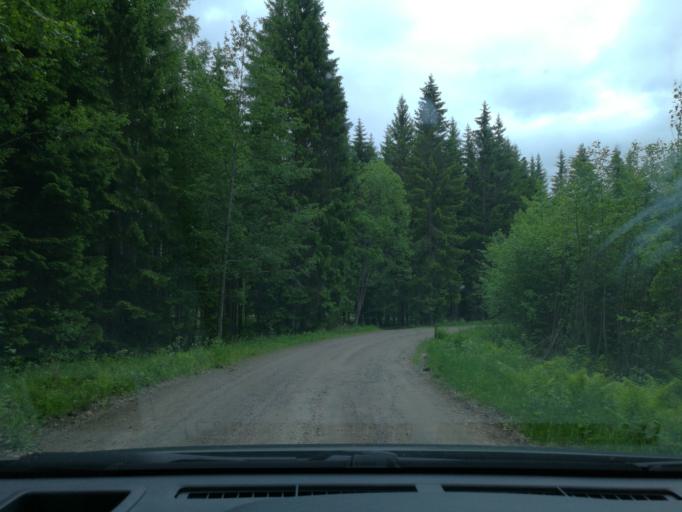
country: SE
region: Dalarna
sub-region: Smedjebackens Kommun
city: Smedjebacken
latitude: 60.1437
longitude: 15.3060
